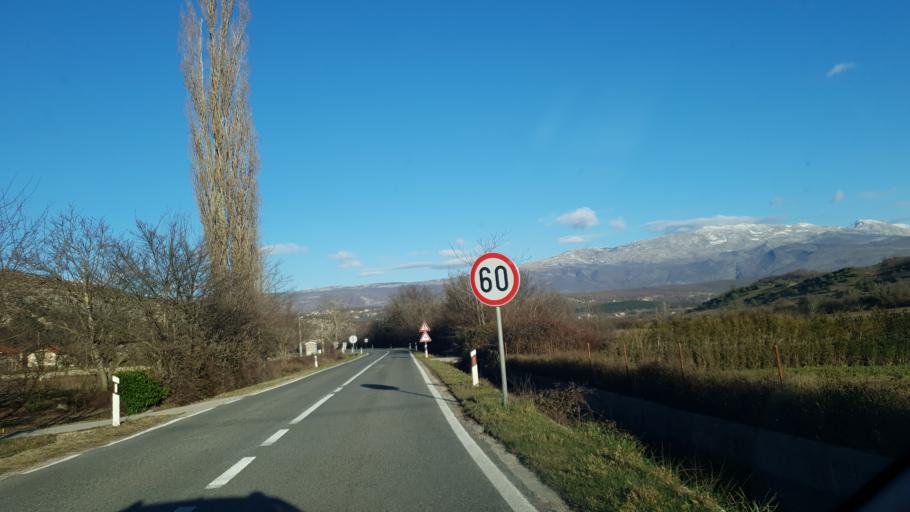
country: HR
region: Splitsko-Dalmatinska
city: Sinj
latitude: 43.7168
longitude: 16.6653
